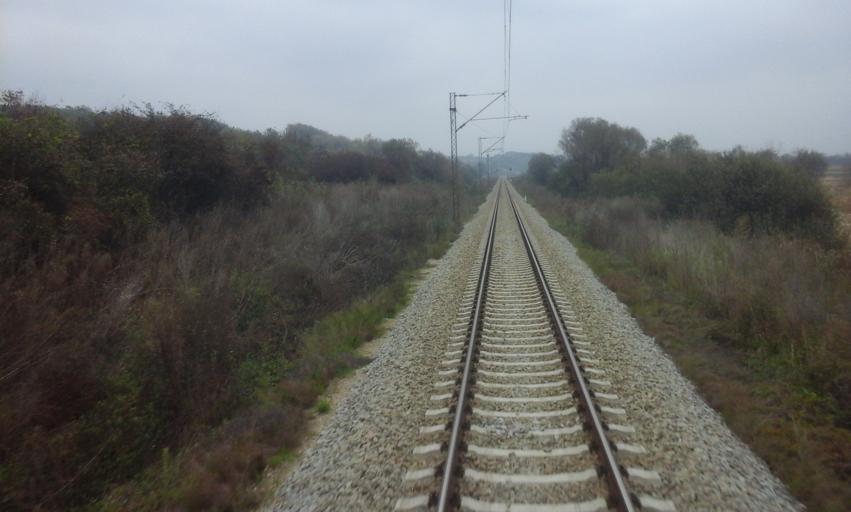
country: RS
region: Central Serbia
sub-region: Belgrade
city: Sopot
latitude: 44.4982
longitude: 20.6466
